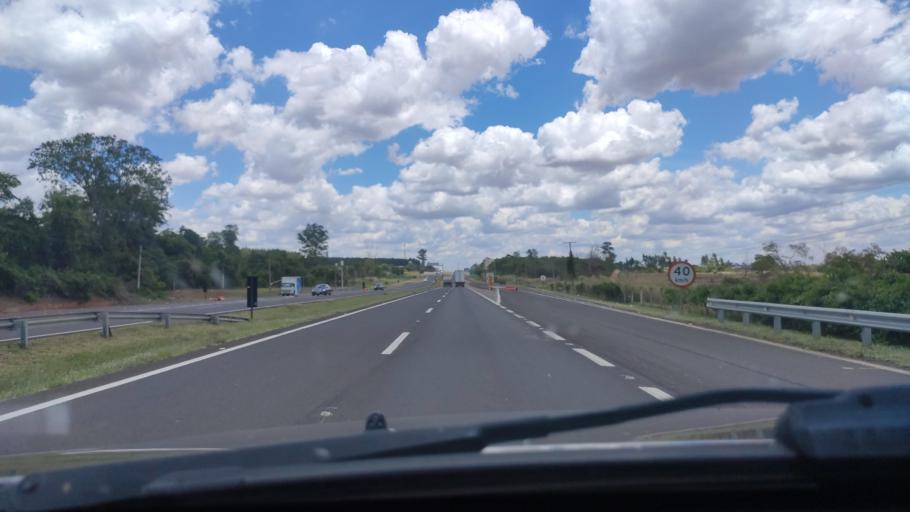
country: BR
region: Sao Paulo
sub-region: Bauru
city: Bauru
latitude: -22.3225
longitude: -48.9636
